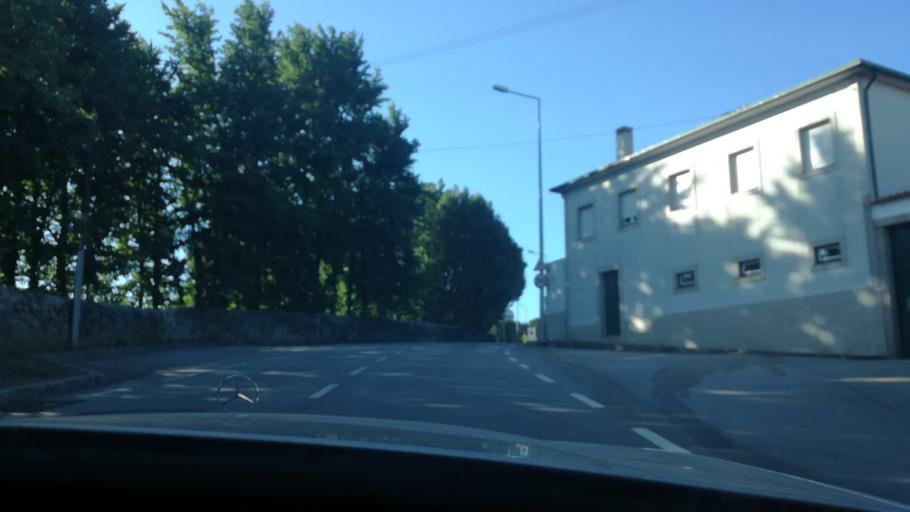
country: PT
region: Porto
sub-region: Maia
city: Leca do Bailio
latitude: 41.2207
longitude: -8.6236
